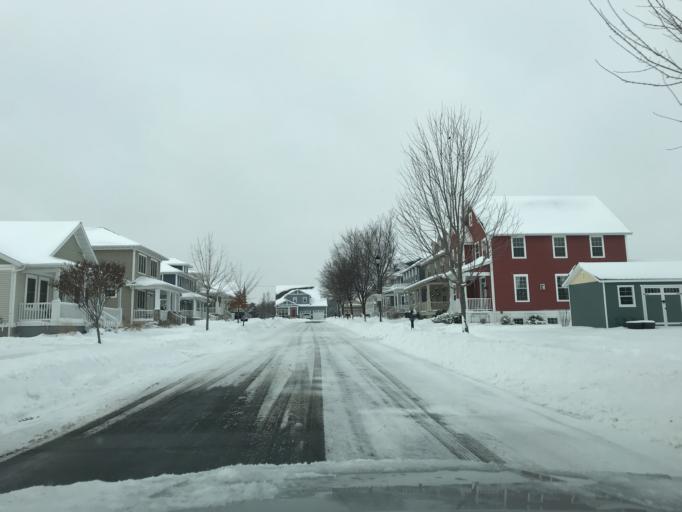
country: US
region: Wisconsin
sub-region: Dane County
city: Sun Prairie
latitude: 43.1658
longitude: -89.2828
